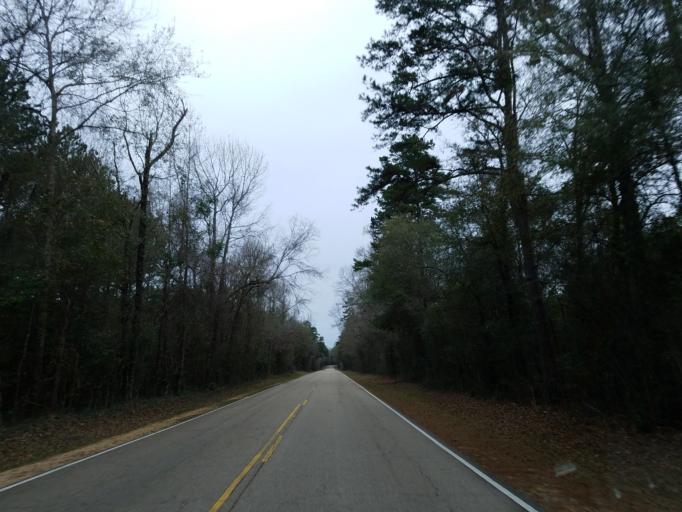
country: US
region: Mississippi
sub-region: Forrest County
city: Hattiesburg
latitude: 31.2492
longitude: -89.2285
